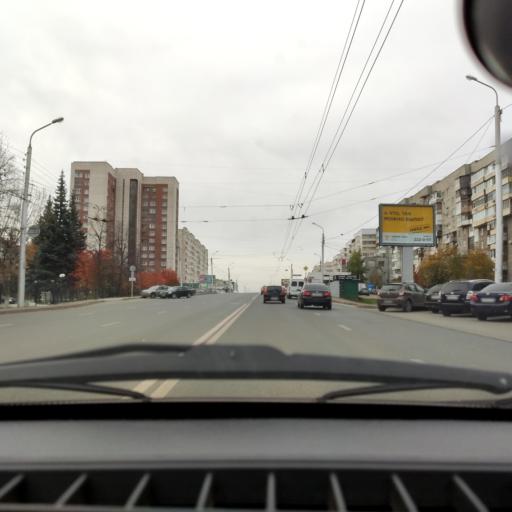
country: RU
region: Bashkortostan
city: Ufa
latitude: 54.7102
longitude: 56.0003
